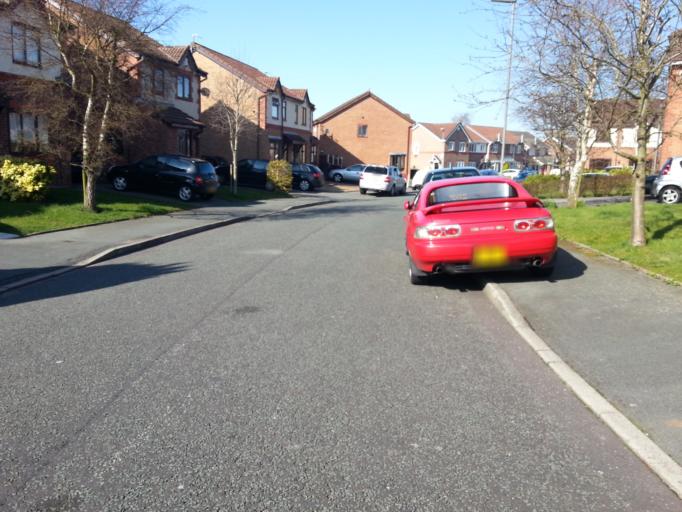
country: GB
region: England
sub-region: Knowsley
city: Huyton
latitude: 53.3690
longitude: -2.8393
